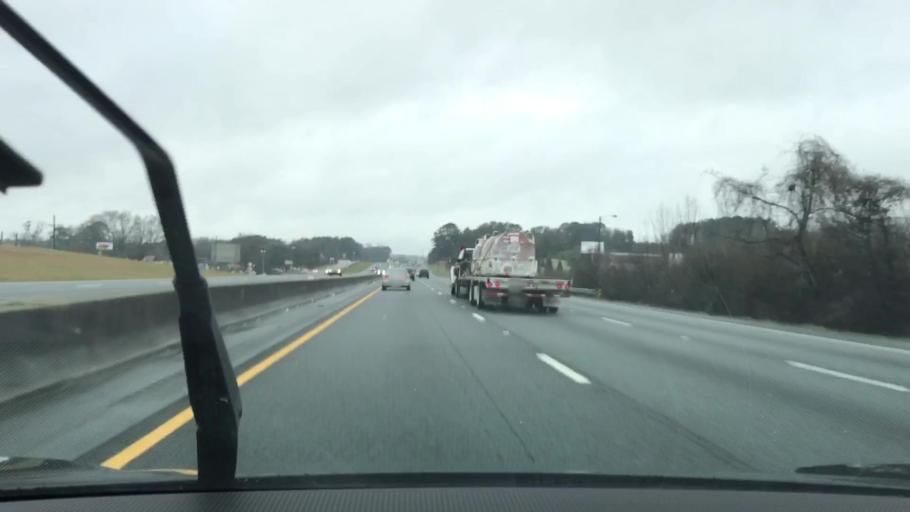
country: US
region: Georgia
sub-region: Newton County
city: Oxford
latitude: 33.6133
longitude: -83.9014
